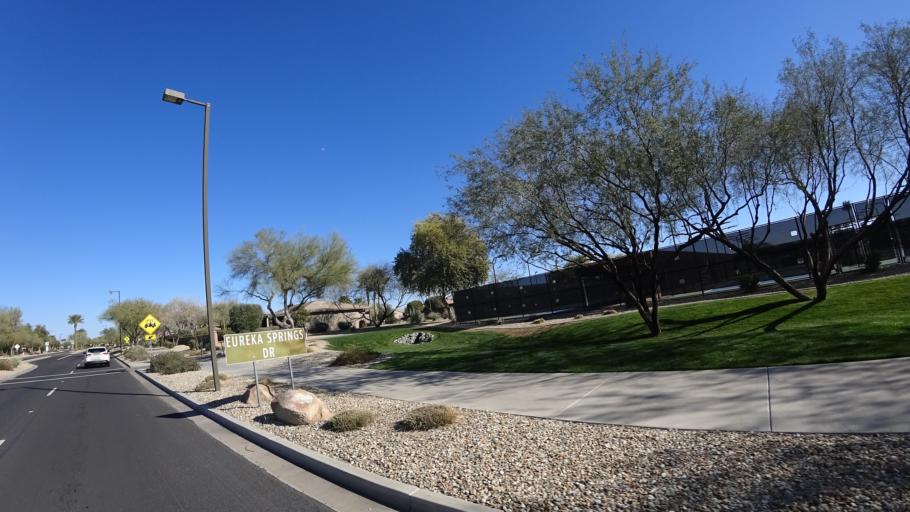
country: US
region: Arizona
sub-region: Maricopa County
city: Sun City West
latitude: 33.6662
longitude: -112.4255
